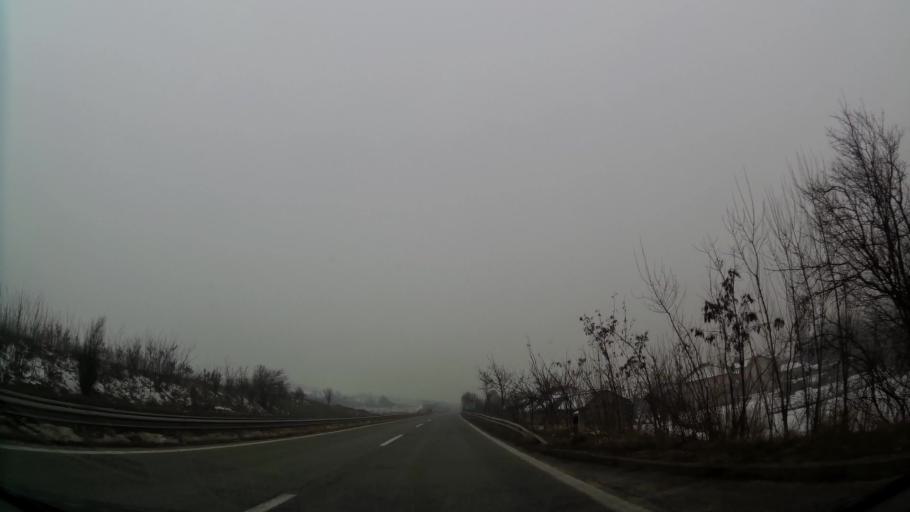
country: MK
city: Miladinovci
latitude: 41.9808
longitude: 21.6528
